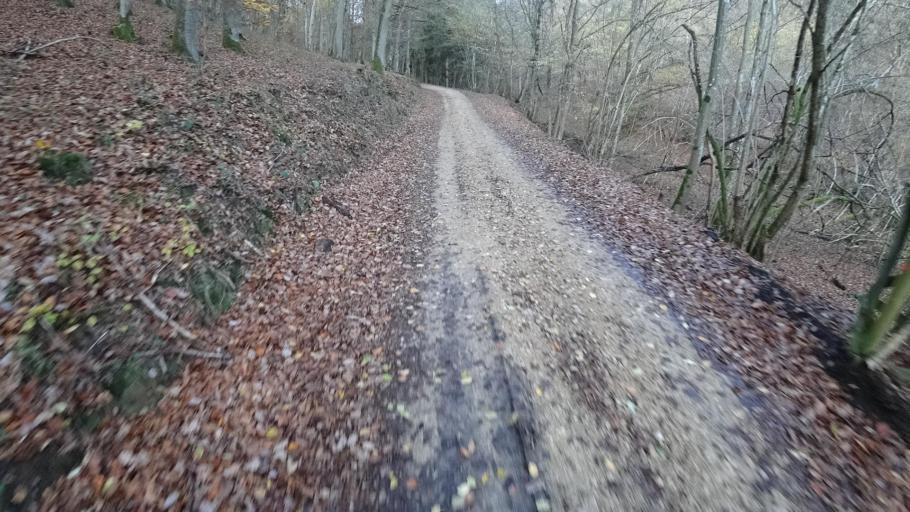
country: DE
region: Rheinland-Pfalz
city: Sierscheid
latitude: 50.4730
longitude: 6.9295
